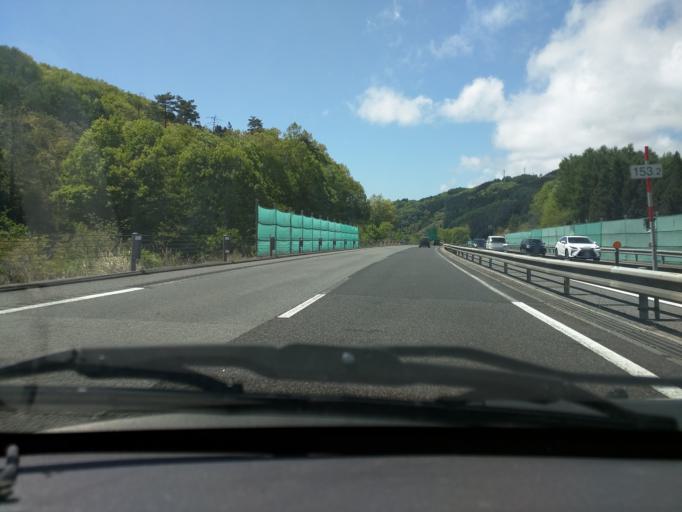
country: JP
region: Nagano
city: Nakano
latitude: 36.7896
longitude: 138.3214
